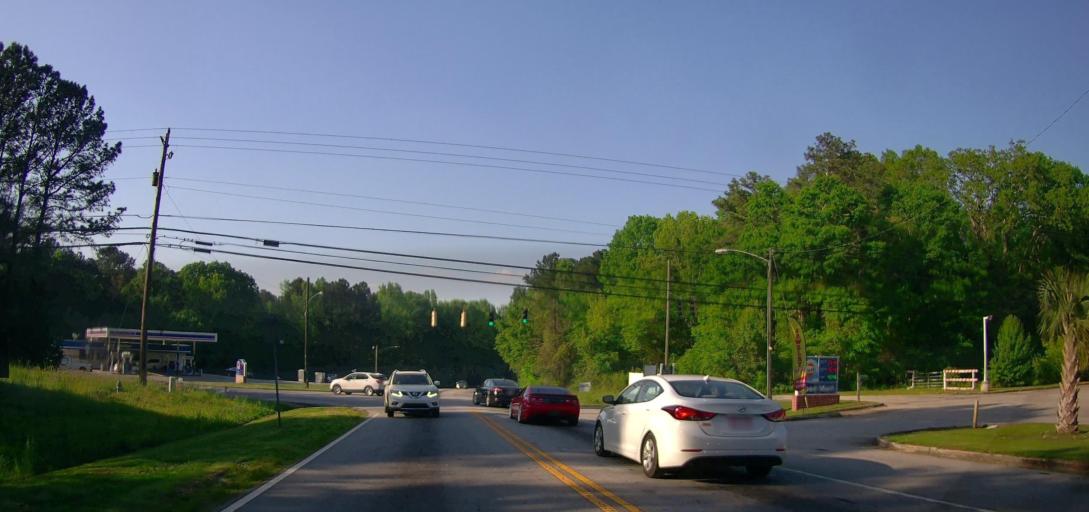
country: US
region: Georgia
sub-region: Newton County
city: Covington
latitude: 33.5934
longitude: -83.8768
